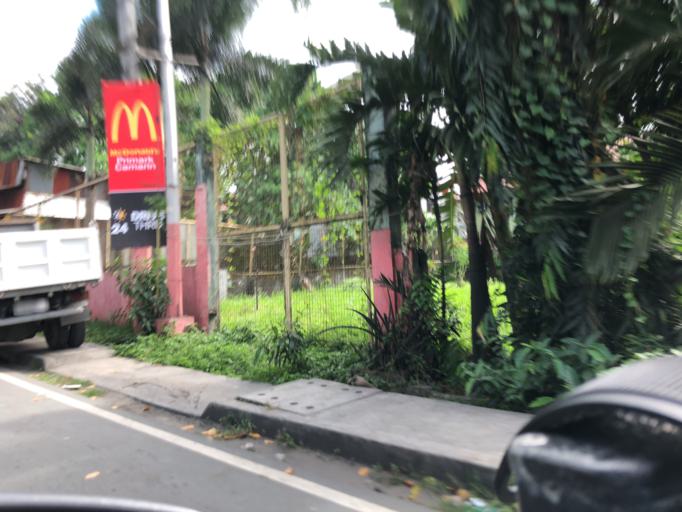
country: PH
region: Central Luzon
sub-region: Province of Bulacan
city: San Jose del Monte
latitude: 14.7585
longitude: 121.0521
